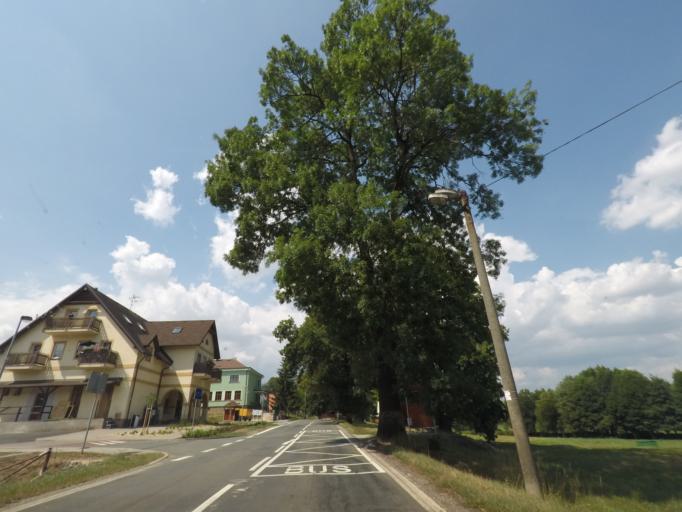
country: CZ
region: Kralovehradecky
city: Zadni Mostek
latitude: 50.5288
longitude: 15.6806
